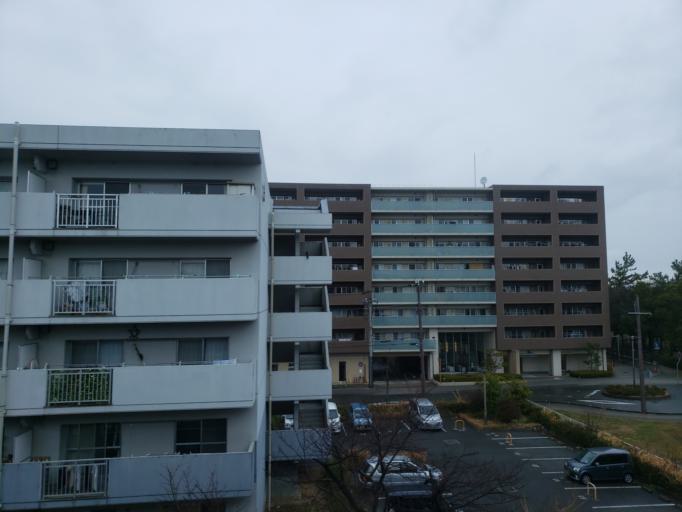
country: JP
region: Hyogo
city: Amagasaki
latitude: 34.7189
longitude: 135.4005
